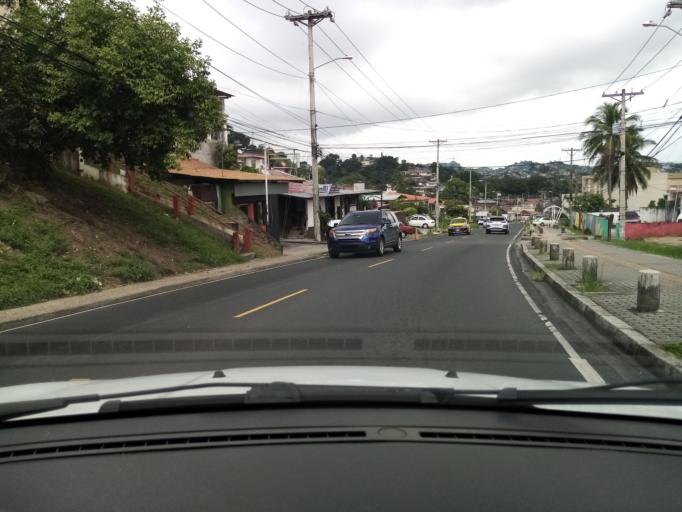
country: PA
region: Panama
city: San Miguelito
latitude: 9.0315
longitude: -79.4922
